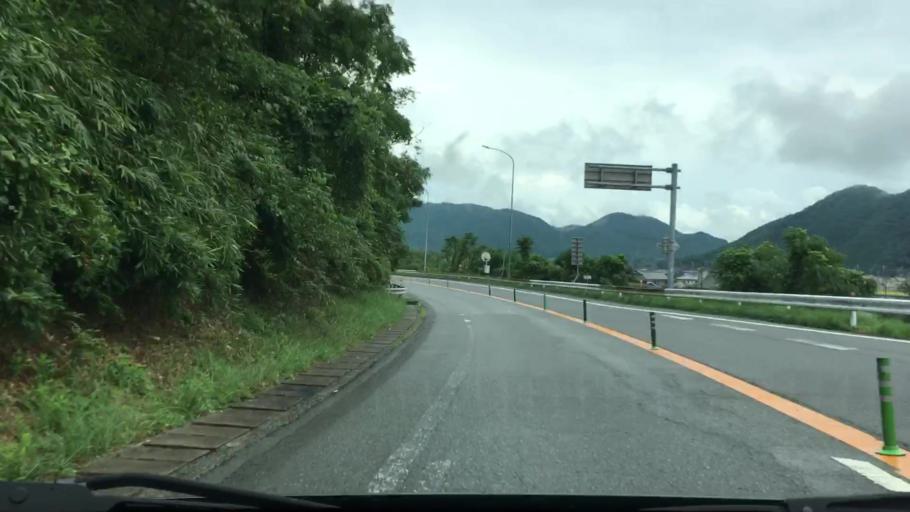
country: JP
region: Hyogo
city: Himeji
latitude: 35.0136
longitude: 134.7605
